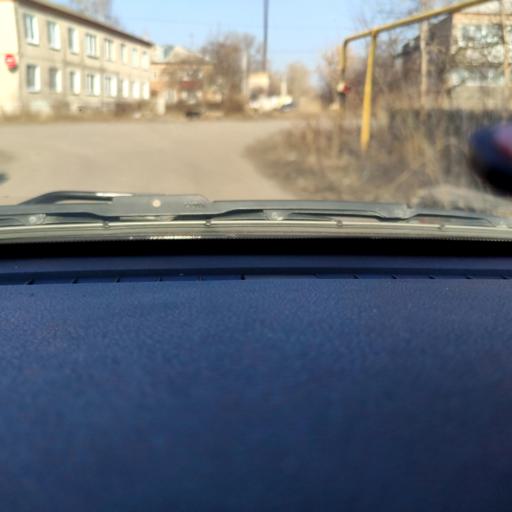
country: RU
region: Voronezj
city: Novaya Usman'
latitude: 51.6439
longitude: 39.4195
